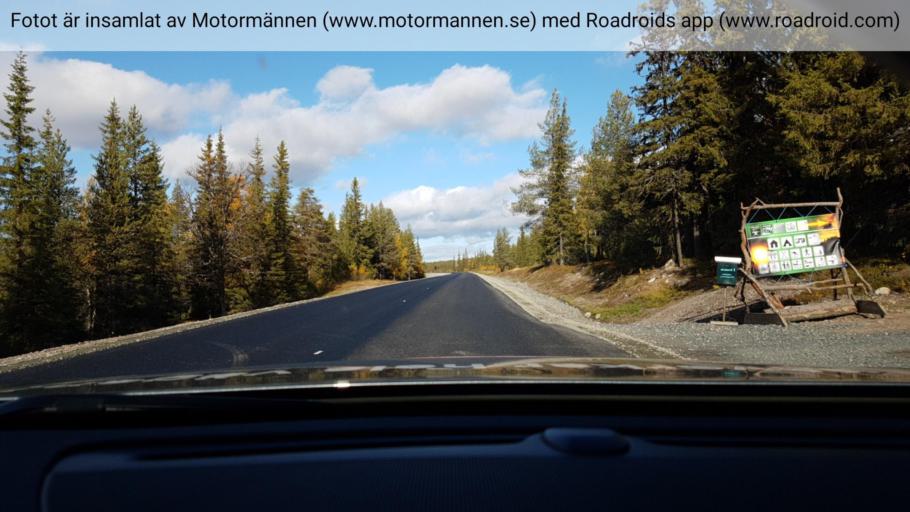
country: SE
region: Norrbotten
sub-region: Arjeplogs Kommun
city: Arjeplog
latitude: 65.9219
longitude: 18.3154
